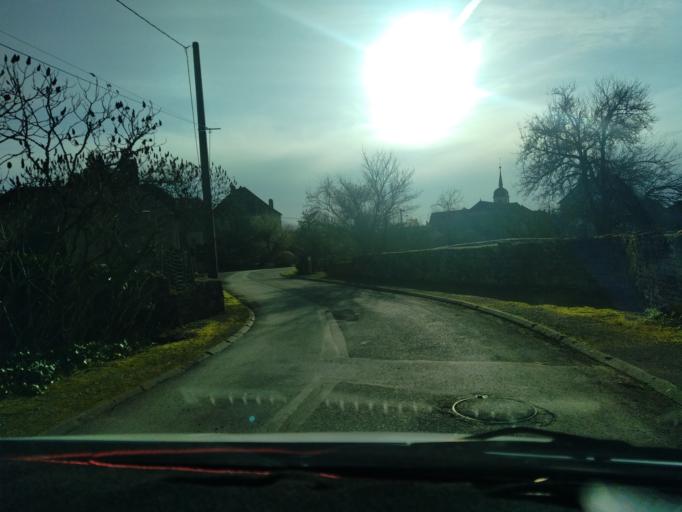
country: FR
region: Franche-Comte
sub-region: Departement de la Haute-Saone
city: Marnay
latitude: 47.3222
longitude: 5.6837
